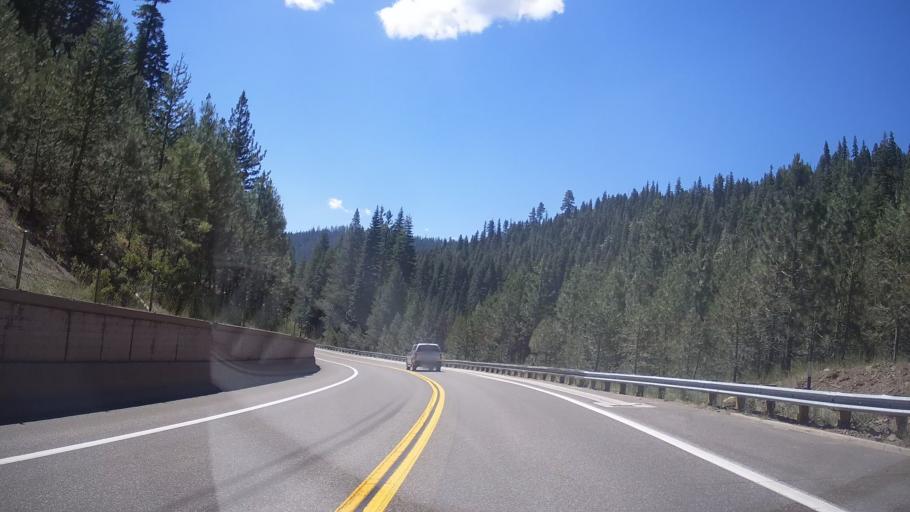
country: US
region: California
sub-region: Placer County
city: Sunnyside-Tahoe City
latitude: 39.1829
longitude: -120.1952
